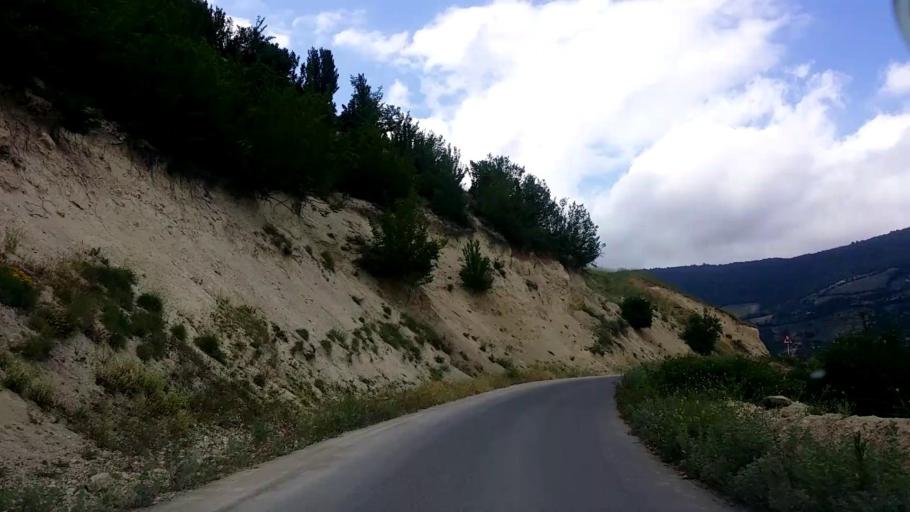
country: IR
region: Mazandaran
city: Chalus
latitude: 36.5410
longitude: 51.2724
